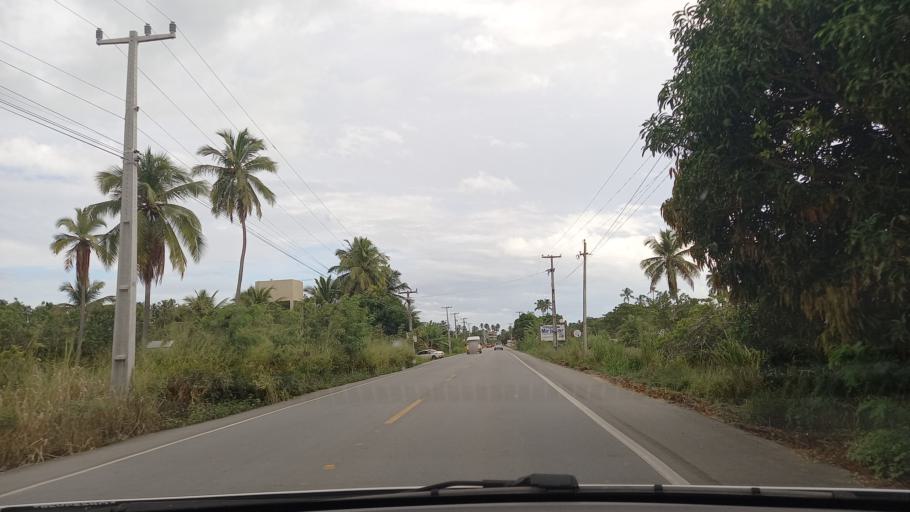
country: BR
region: Alagoas
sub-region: Maragogi
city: Maragogi
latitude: -8.9720
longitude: -35.1833
